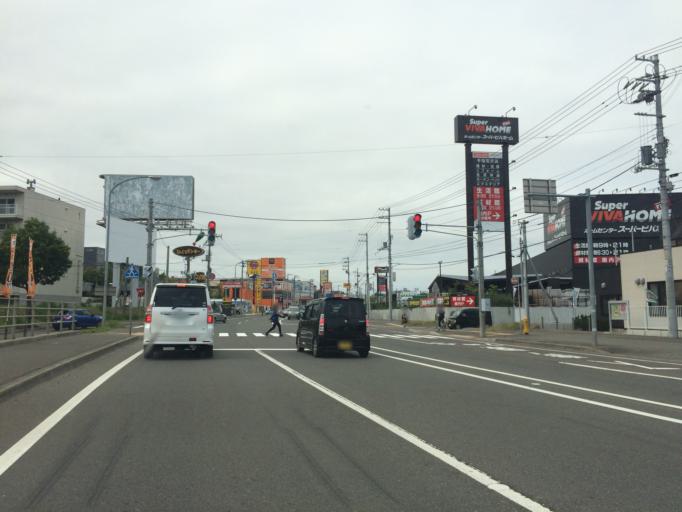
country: JP
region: Hokkaido
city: Sapporo
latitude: 43.0990
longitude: 141.2547
